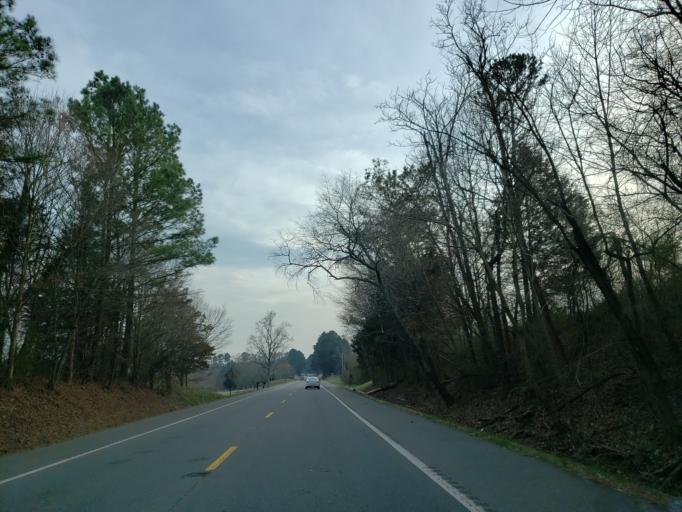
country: US
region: Tennessee
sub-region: Bradley County
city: Wildwood Lake
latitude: 35.0401
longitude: -84.9052
